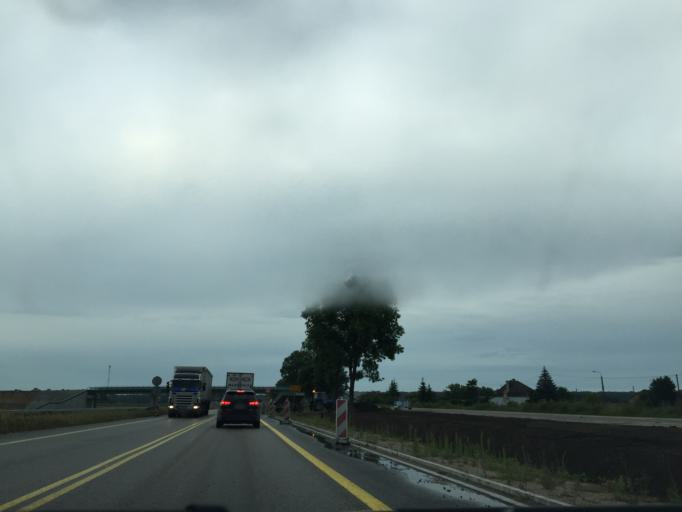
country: PL
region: Podlasie
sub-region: Powiat zambrowski
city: Szumowo
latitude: 52.9199
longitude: 22.1156
